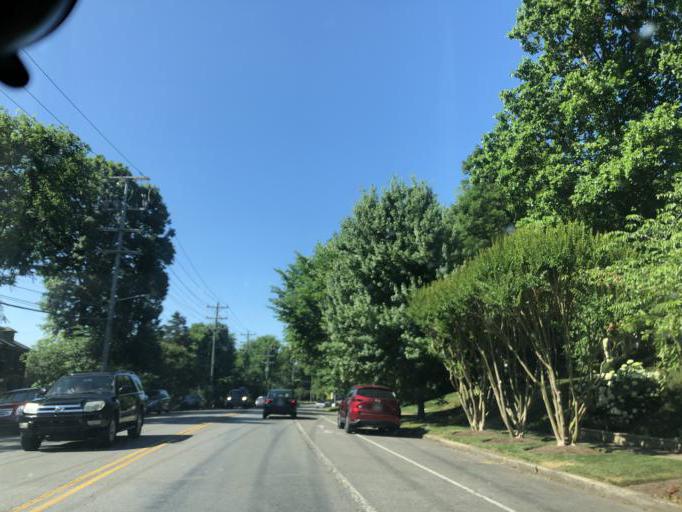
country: US
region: Tennessee
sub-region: Davidson County
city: Oak Hill
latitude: 36.1215
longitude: -86.7949
